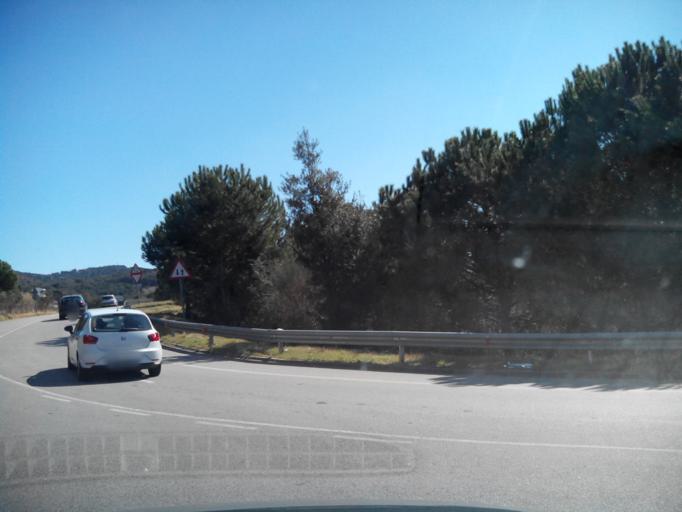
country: ES
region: Catalonia
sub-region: Provincia de Barcelona
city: Argentona
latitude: 41.5724
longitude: 2.3885
